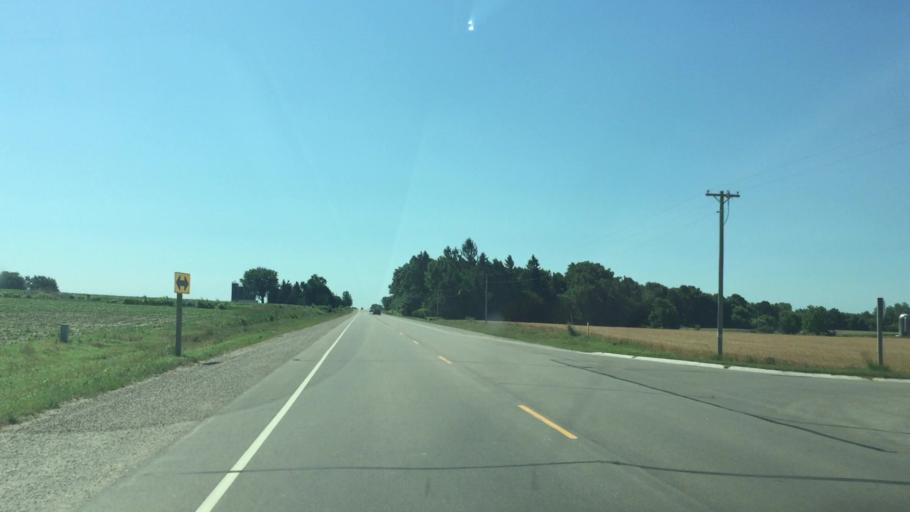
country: US
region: Wisconsin
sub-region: Calumet County
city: Chilton
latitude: 43.9964
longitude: -88.1292
